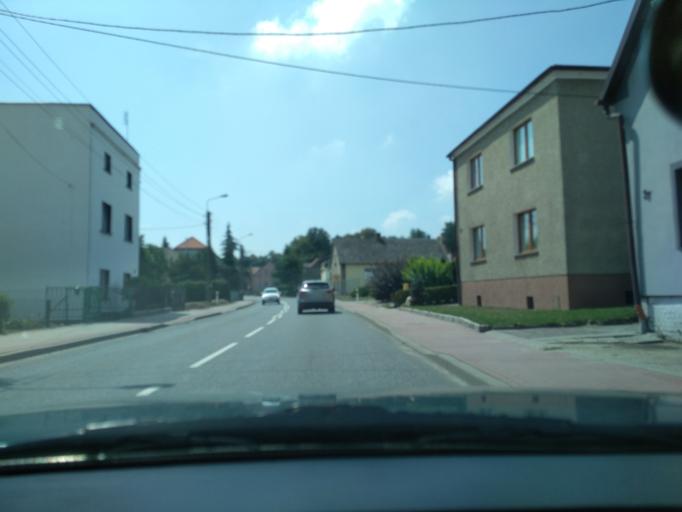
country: PL
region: Silesian Voivodeship
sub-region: Powiat raciborski
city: Raciborz
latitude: 50.0959
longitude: 18.2028
